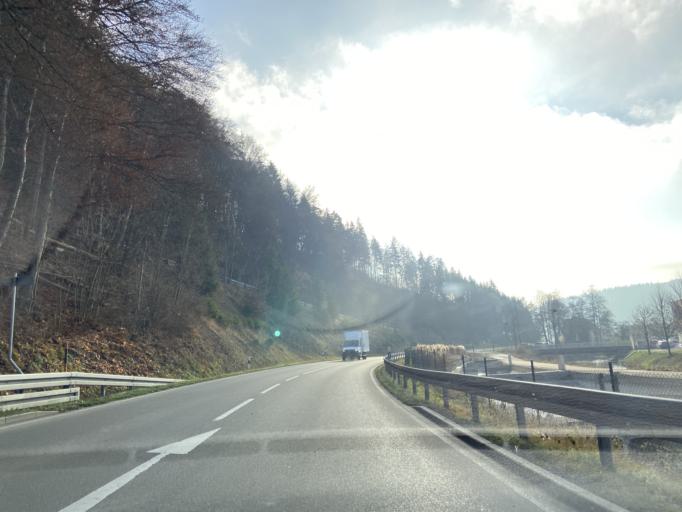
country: DE
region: Baden-Wuerttemberg
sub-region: Tuebingen Region
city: Hettingen
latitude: 48.2235
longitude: 9.2373
